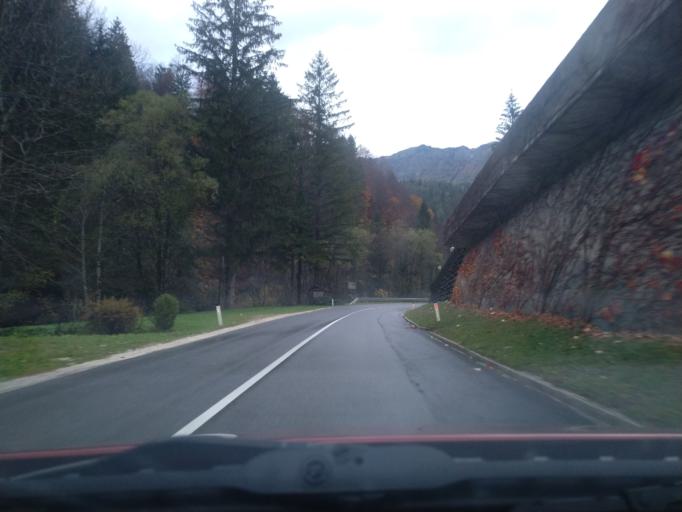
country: SI
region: Solcava
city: Solcava
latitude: 46.4131
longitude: 14.7007
